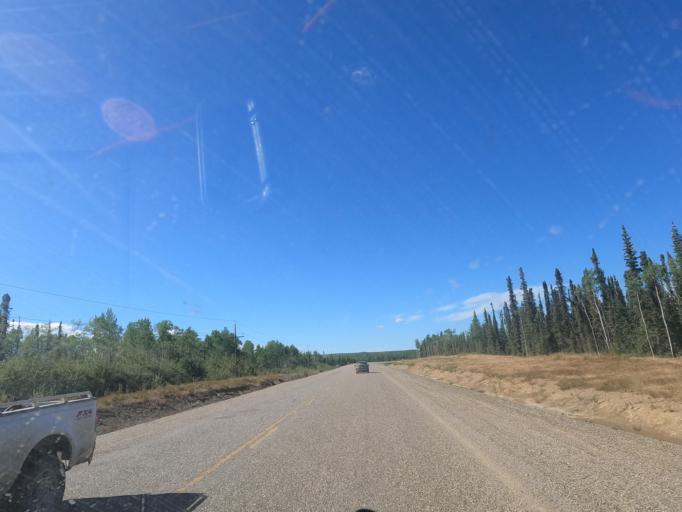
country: CA
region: Yukon
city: Dawson City
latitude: 63.8733
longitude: -138.1308
